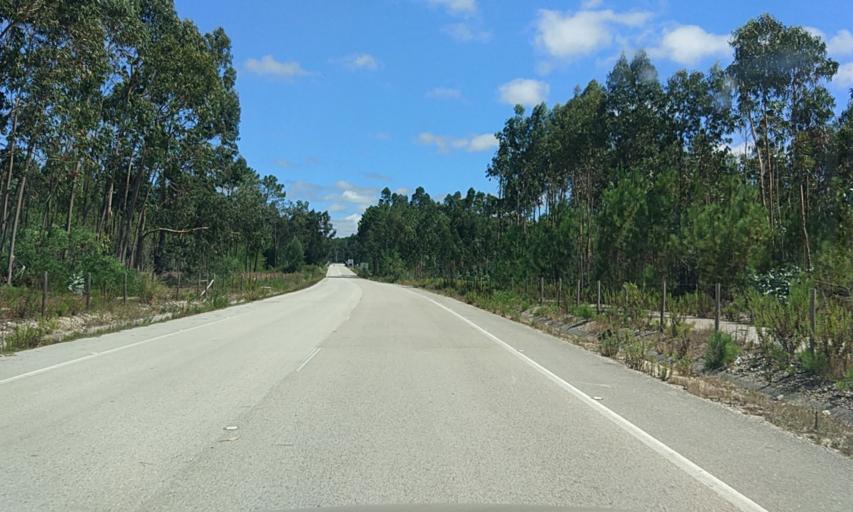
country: PT
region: Coimbra
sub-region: Mira
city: Mira
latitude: 40.3375
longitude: -8.7390
